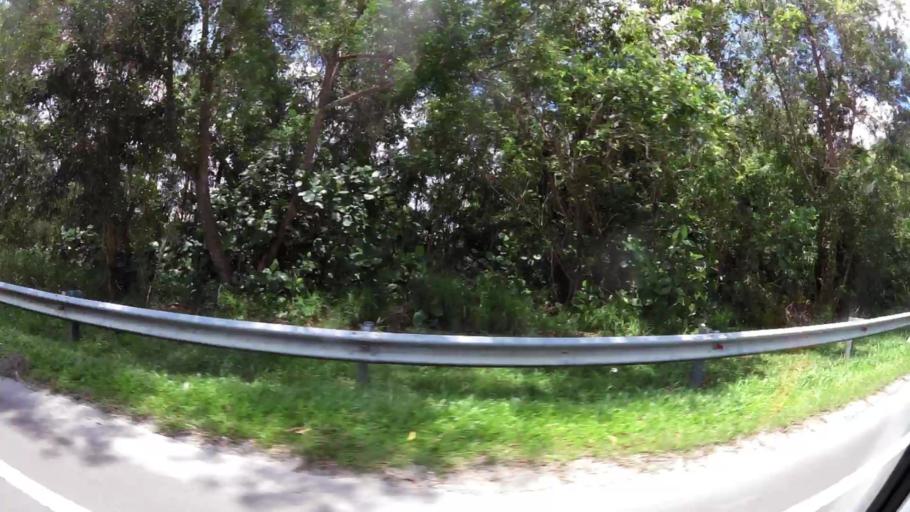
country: BN
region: Brunei and Muara
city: Bandar Seri Begawan
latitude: 4.9266
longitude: 114.9626
